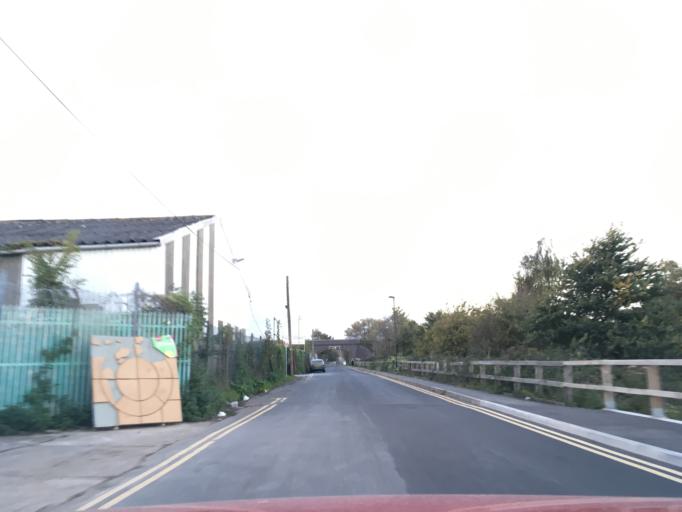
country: GB
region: England
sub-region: South Gloucestershire
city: Stoke Gifford
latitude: 51.5270
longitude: -2.5626
